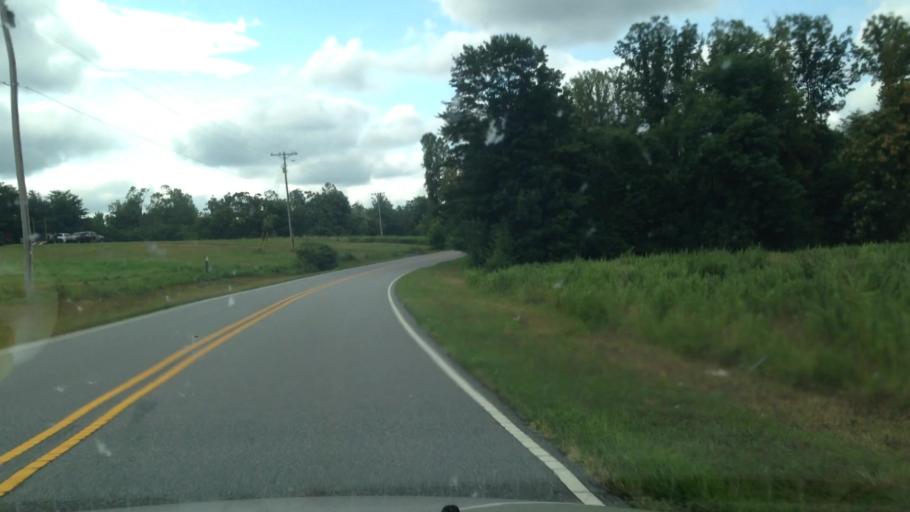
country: US
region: North Carolina
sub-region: Rockingham County
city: Mayodan
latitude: 36.4194
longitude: -80.0691
